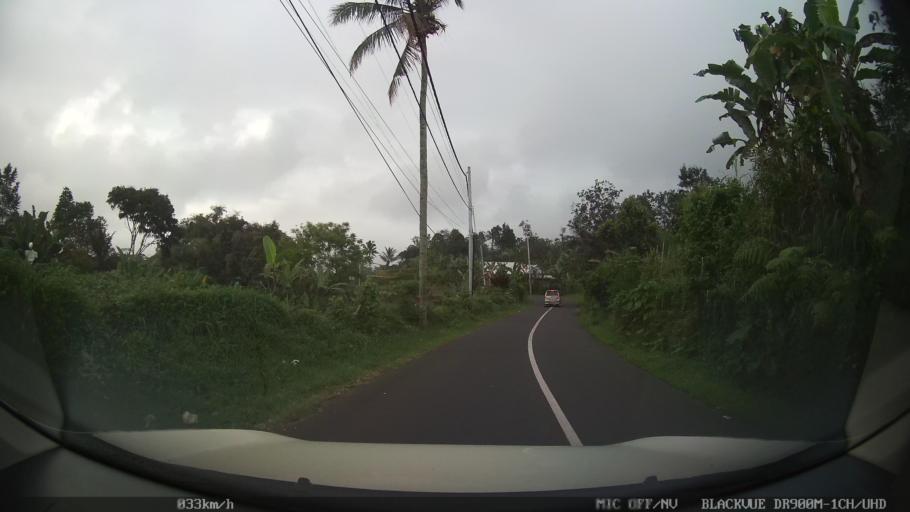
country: ID
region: Bali
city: Peneng
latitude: -8.3407
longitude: 115.1878
